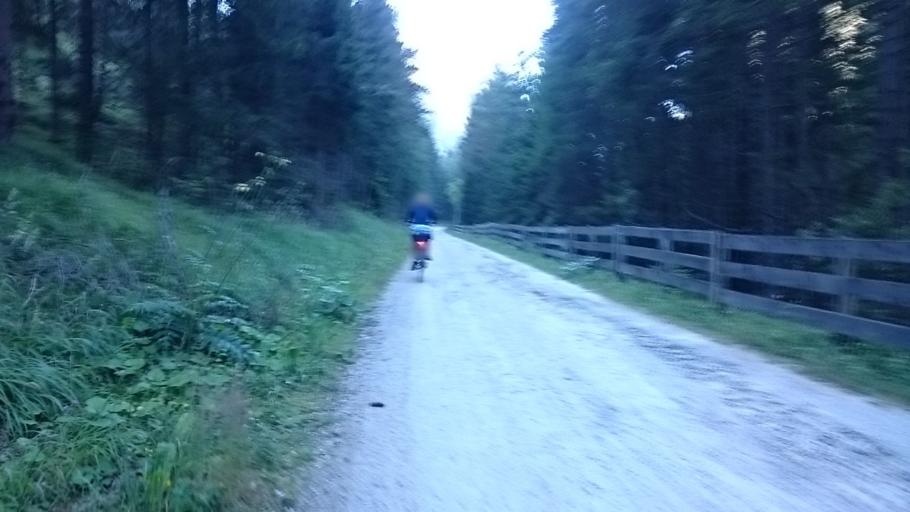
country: IT
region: Trentino-Alto Adige
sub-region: Bolzano
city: Dobbiaco
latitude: 46.6964
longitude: 12.2219
